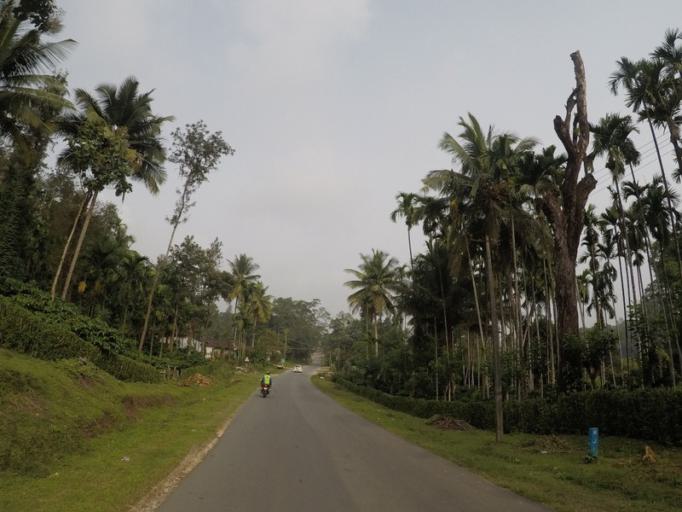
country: IN
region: Karnataka
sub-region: Chikmagalur
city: Chikmagalur
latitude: 13.3370
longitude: 75.5492
